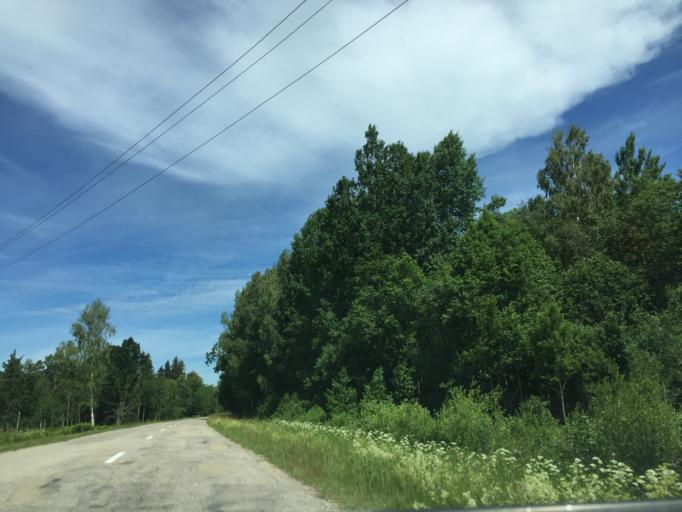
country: LV
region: Dundaga
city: Dundaga
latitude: 57.5685
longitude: 22.3074
